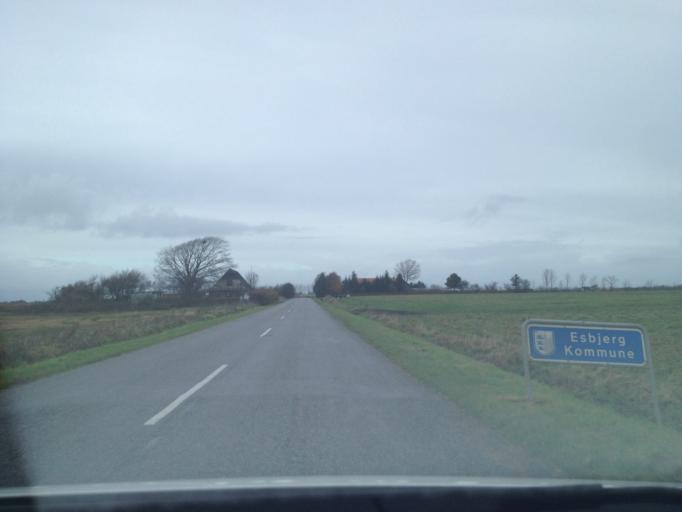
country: DK
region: South Denmark
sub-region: Tonder Kommune
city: Sherrebek
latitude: 55.2275
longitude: 8.8353
